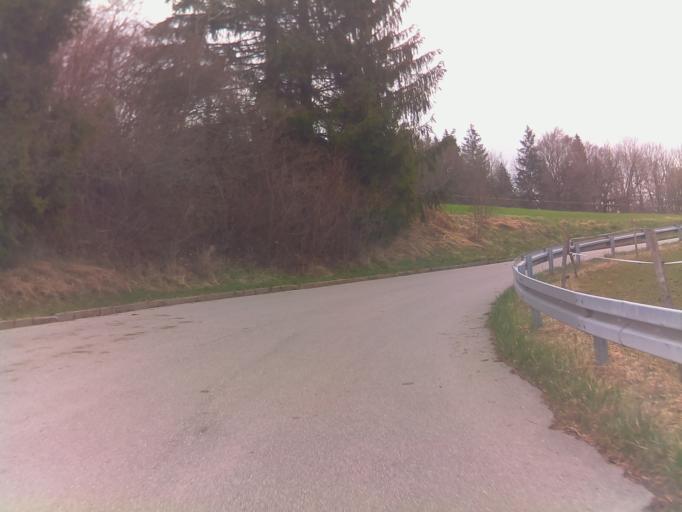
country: DE
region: Bavaria
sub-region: Upper Bavaria
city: Hohenpeissenberg
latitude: 47.7818
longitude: 11.0353
